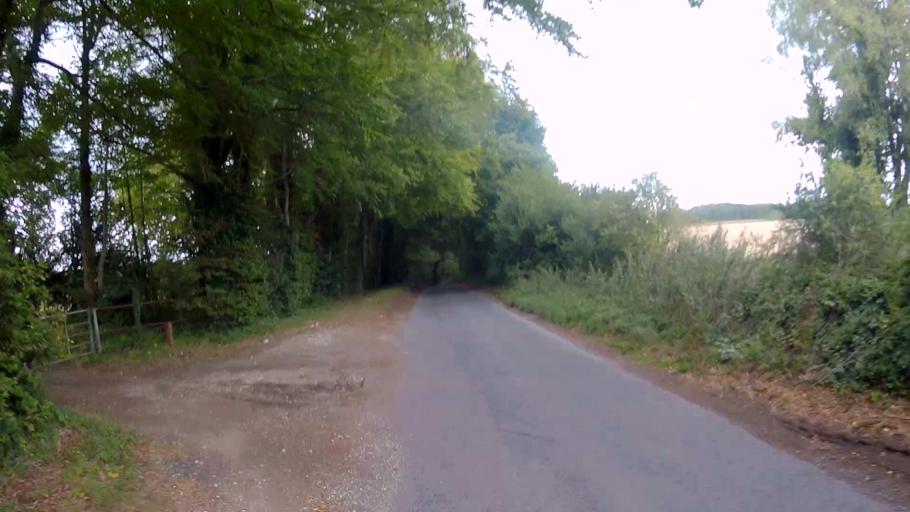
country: GB
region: England
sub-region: Hampshire
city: Overton
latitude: 51.1875
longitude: -1.2769
